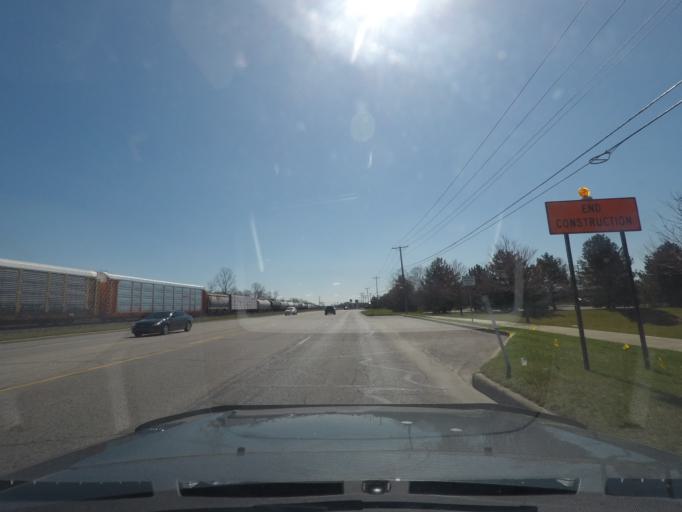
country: US
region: Indiana
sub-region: Elkhart County
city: Dunlap
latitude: 41.6257
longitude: -85.9048
